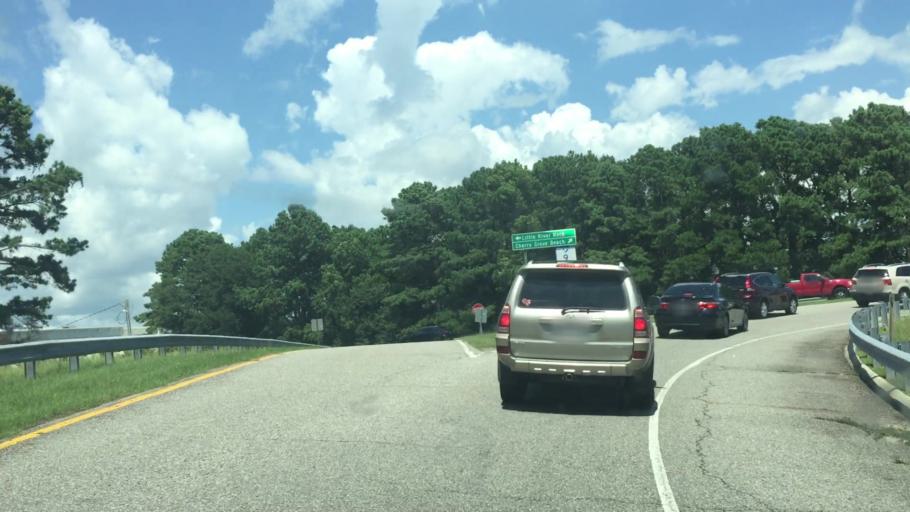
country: US
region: South Carolina
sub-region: Horry County
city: North Myrtle Beach
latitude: 33.8478
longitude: -78.6542
